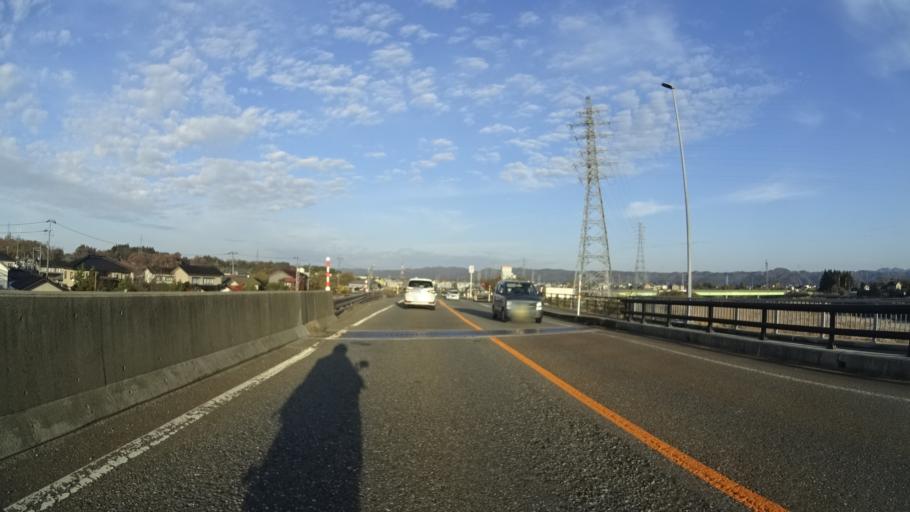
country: JP
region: Niigata
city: Kashiwazaki
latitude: 37.3898
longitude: 138.5933
